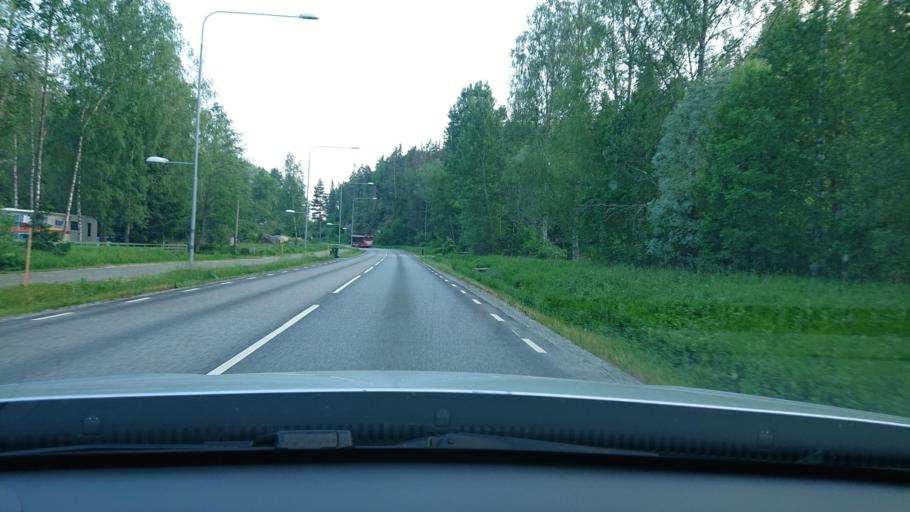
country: SE
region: Stockholm
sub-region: Vaxholms Kommun
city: Resaro
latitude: 59.4823
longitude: 18.3891
